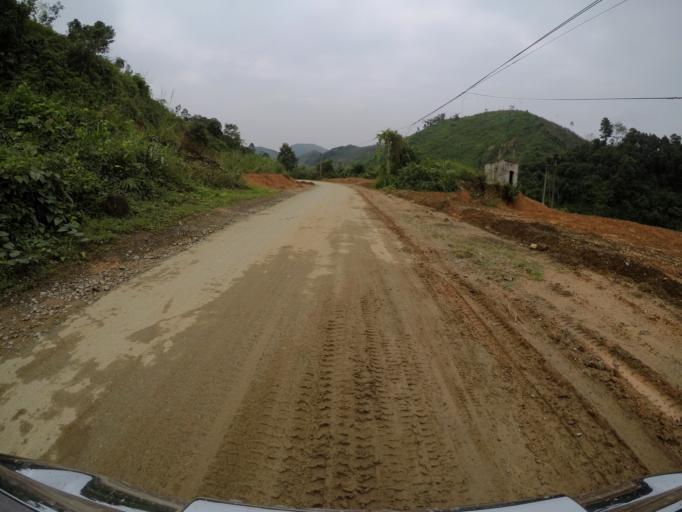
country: VN
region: Yen Bai
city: Co Phuc
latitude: 21.8529
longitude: 104.6184
